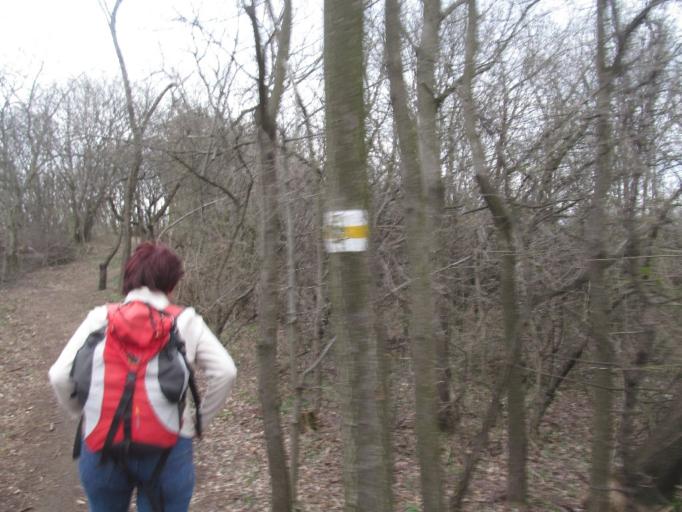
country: HU
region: Gyor-Moson-Sopron
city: Pannonhalma
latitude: 47.5476
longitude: 17.7650
